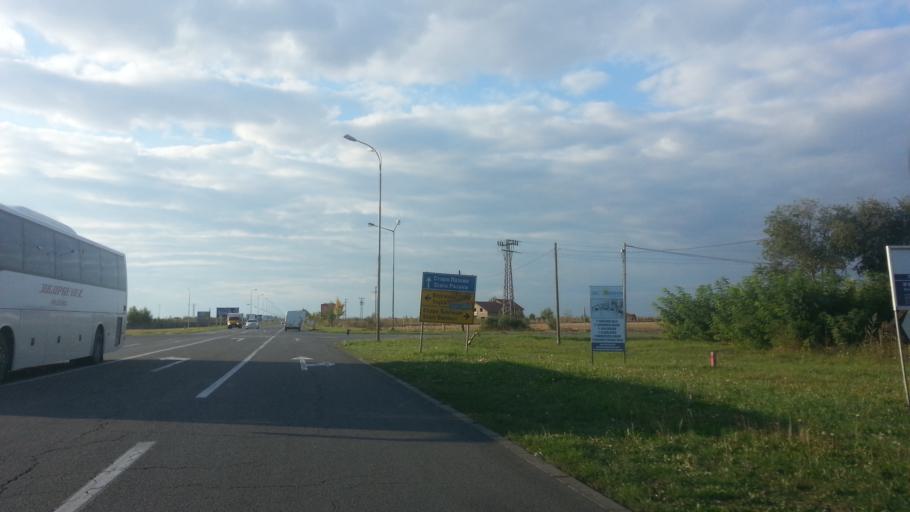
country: RS
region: Autonomna Pokrajina Vojvodina
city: Nova Pazova
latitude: 44.9563
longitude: 20.2016
